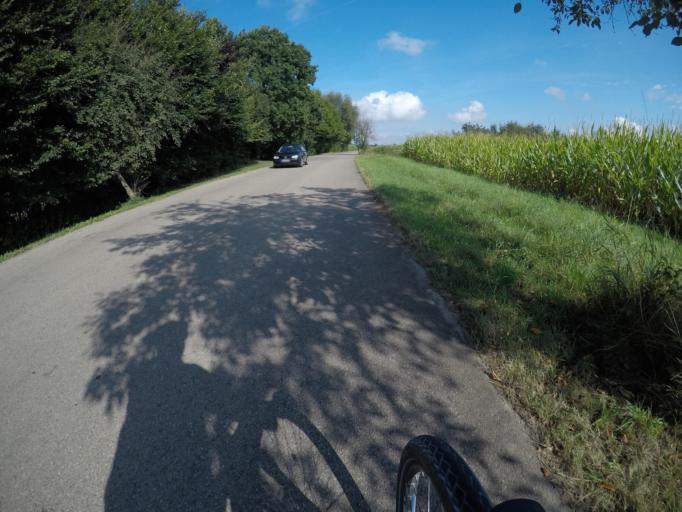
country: DE
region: Bavaria
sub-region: Swabia
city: Buttenwiesen
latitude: 48.6459
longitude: 10.7333
